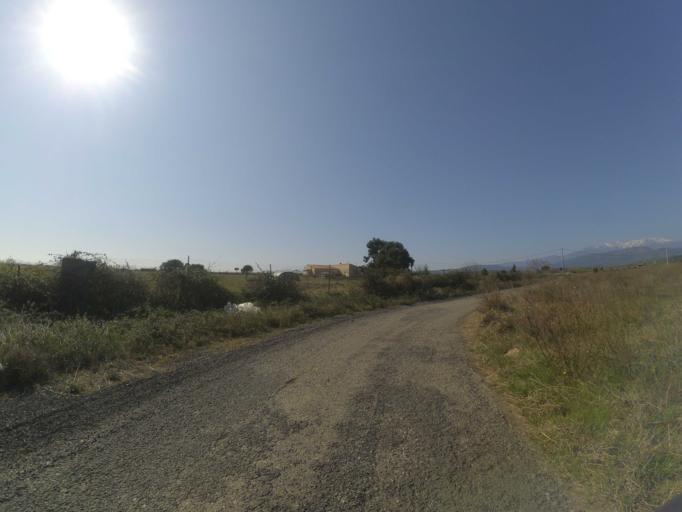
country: FR
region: Languedoc-Roussillon
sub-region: Departement des Pyrenees-Orientales
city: Llupia
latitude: 42.6097
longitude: 2.7596
